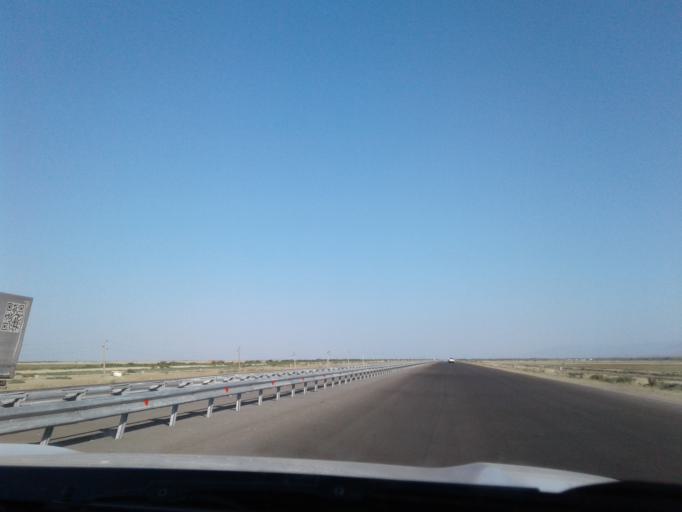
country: TM
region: Balkan
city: Serdar
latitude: 38.9010
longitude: 56.5102
